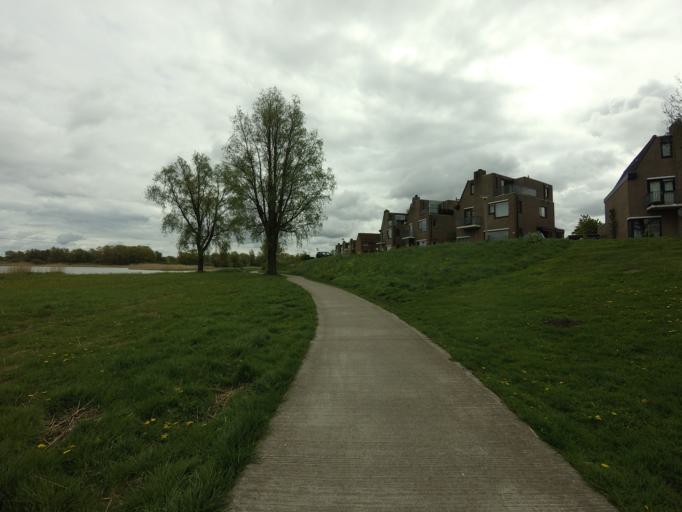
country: NL
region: North Holland
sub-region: Gemeente Naarden
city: Naarden
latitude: 52.3275
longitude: 5.1250
